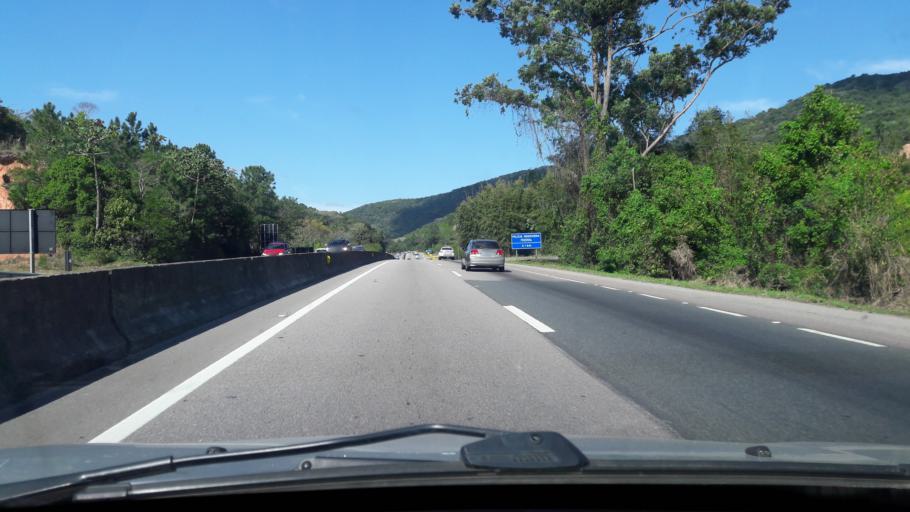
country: BR
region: Santa Catarina
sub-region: Biguacu
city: Biguacu
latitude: -27.4600
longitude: -48.6393
